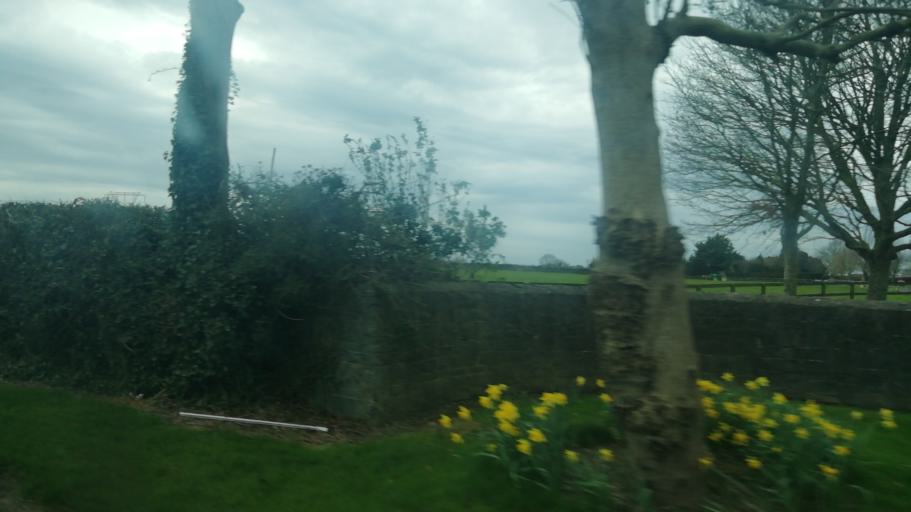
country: IE
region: Leinster
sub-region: Kildare
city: Kilcock
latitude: 53.3477
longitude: -6.6488
